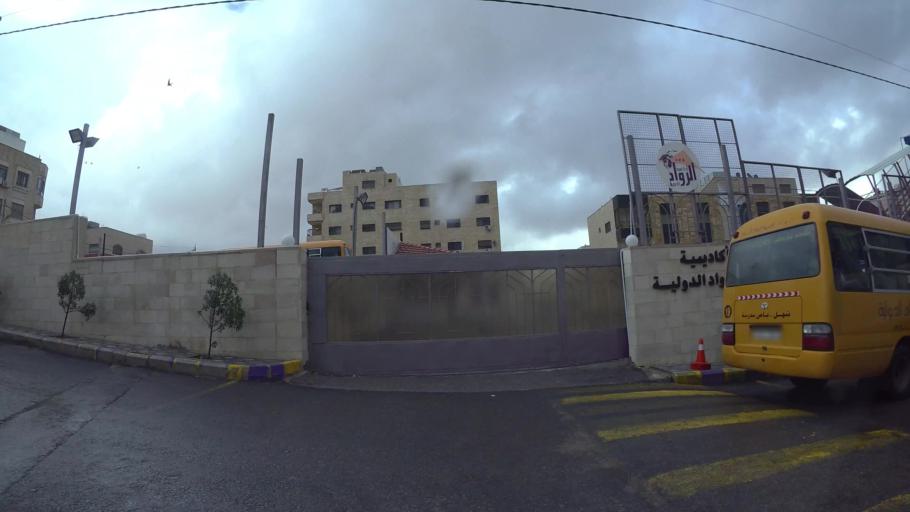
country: JO
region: Amman
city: Al Jubayhah
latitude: 32.0357
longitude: 35.8902
